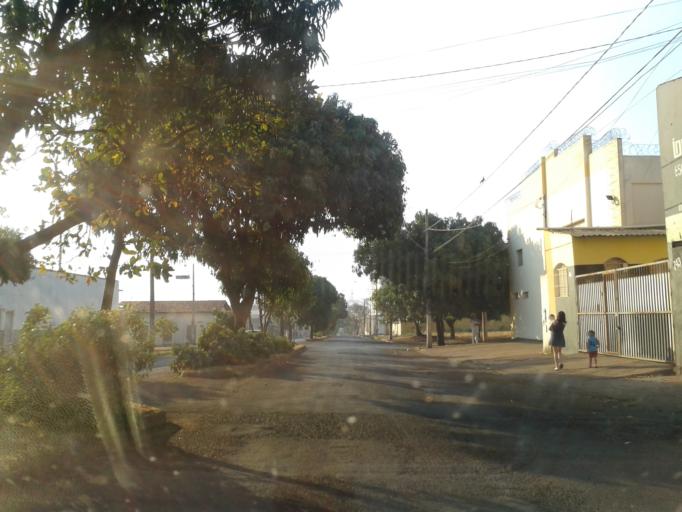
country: BR
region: Minas Gerais
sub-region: Uberlandia
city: Uberlandia
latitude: -18.8994
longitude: -48.2477
